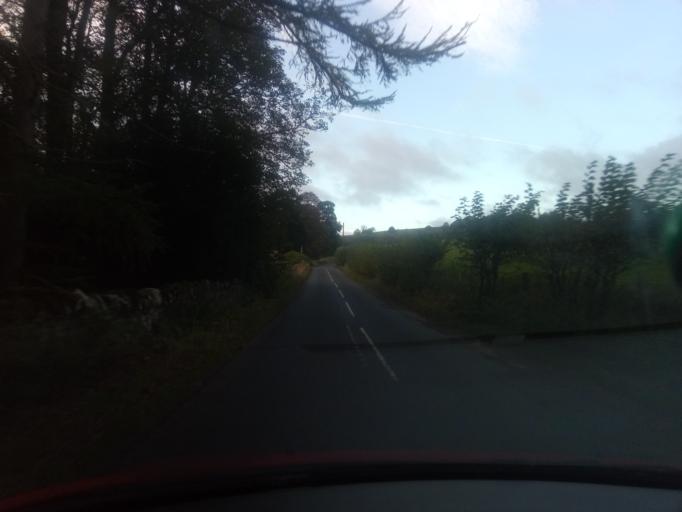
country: GB
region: Scotland
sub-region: The Scottish Borders
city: Jedburgh
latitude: 55.4095
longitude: -2.6511
